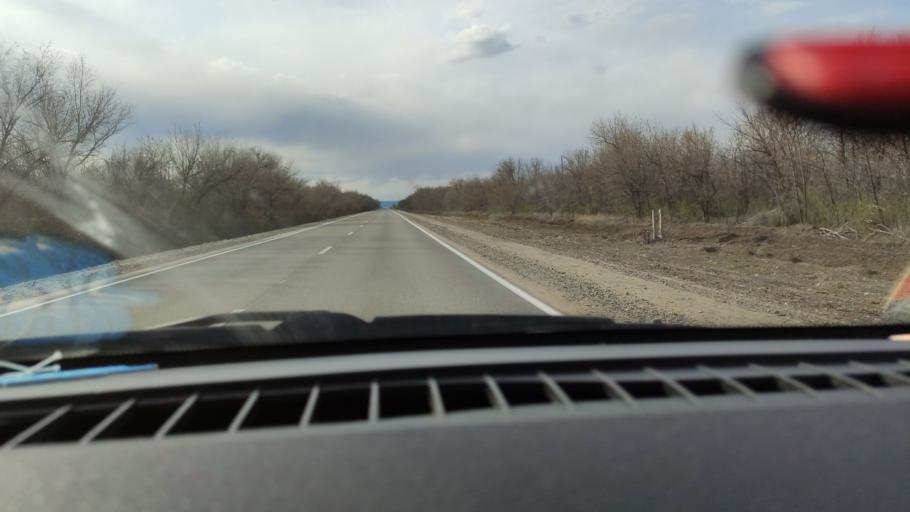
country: RU
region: Saratov
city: Privolzhskiy
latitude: 51.1746
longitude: 45.9313
